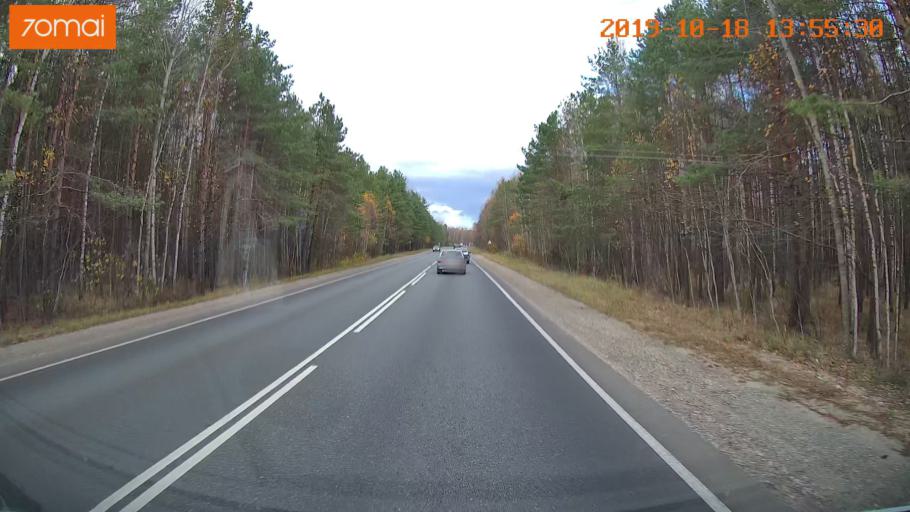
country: RU
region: Rjazan
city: Spas-Klepiki
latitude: 55.0530
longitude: 40.0237
